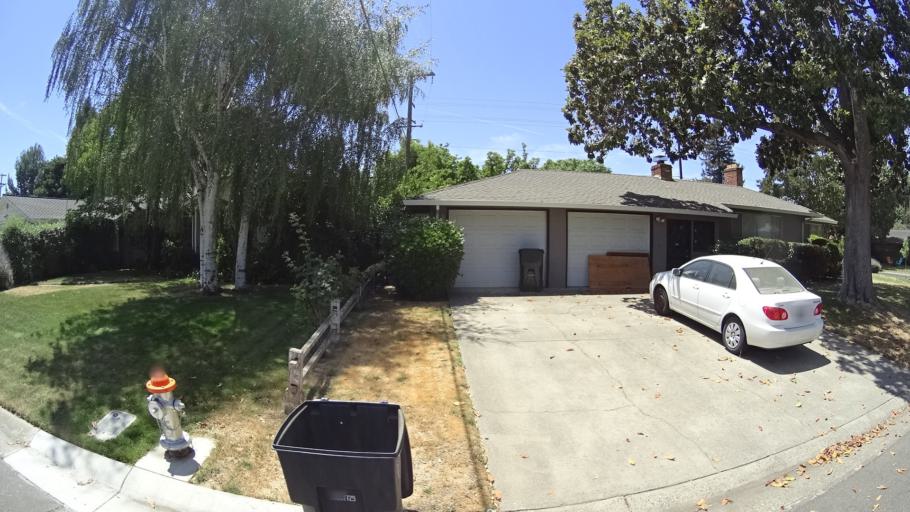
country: US
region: California
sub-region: Yolo County
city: West Sacramento
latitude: 38.5239
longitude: -121.5178
